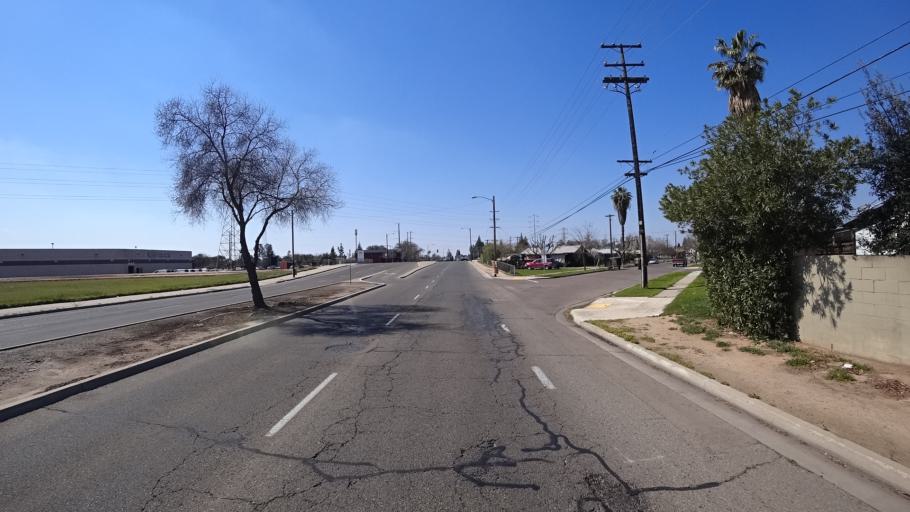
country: US
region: California
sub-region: Fresno County
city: Fresno
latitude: 36.7938
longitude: -119.8244
